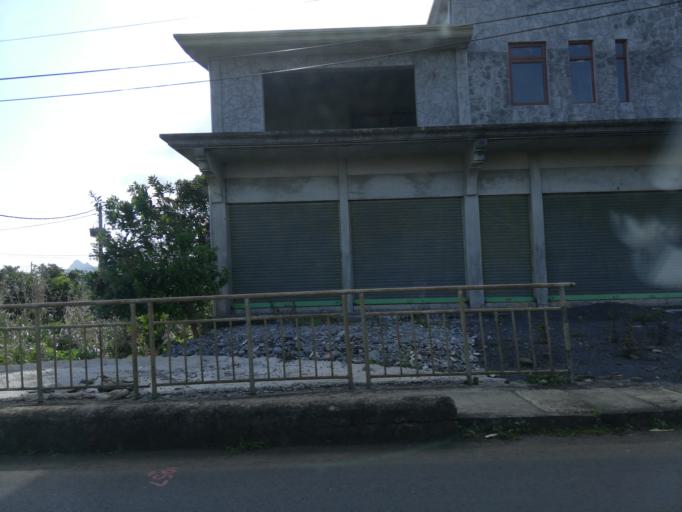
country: MU
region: Moka
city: Verdun
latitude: -20.2208
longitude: 57.5484
